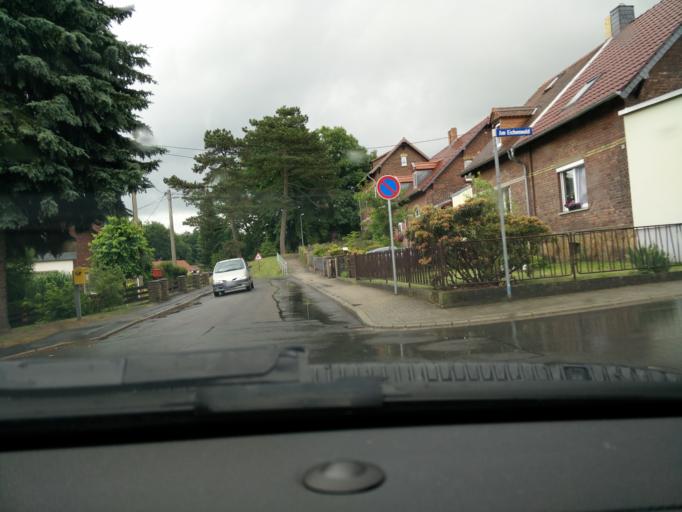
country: DE
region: Saxony
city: Nerchau
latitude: 51.2512
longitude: 12.7693
